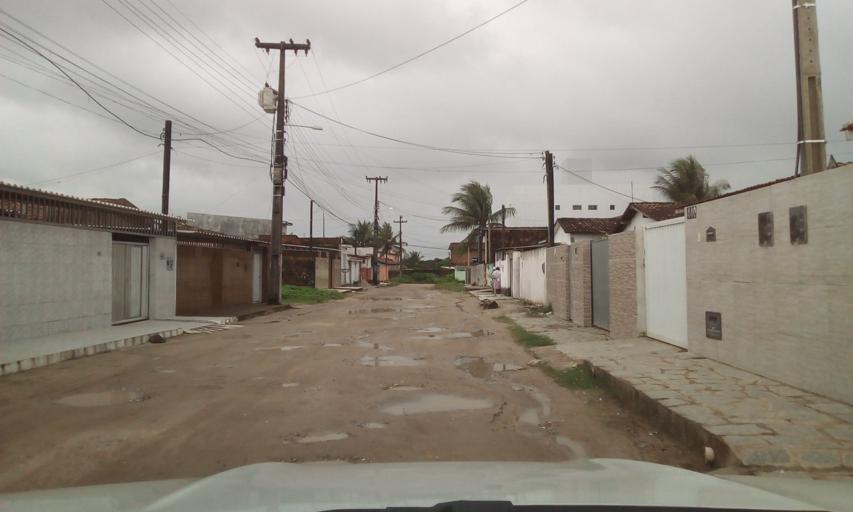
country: BR
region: Paraiba
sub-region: Bayeux
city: Bayeux
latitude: -7.1772
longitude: -34.9270
